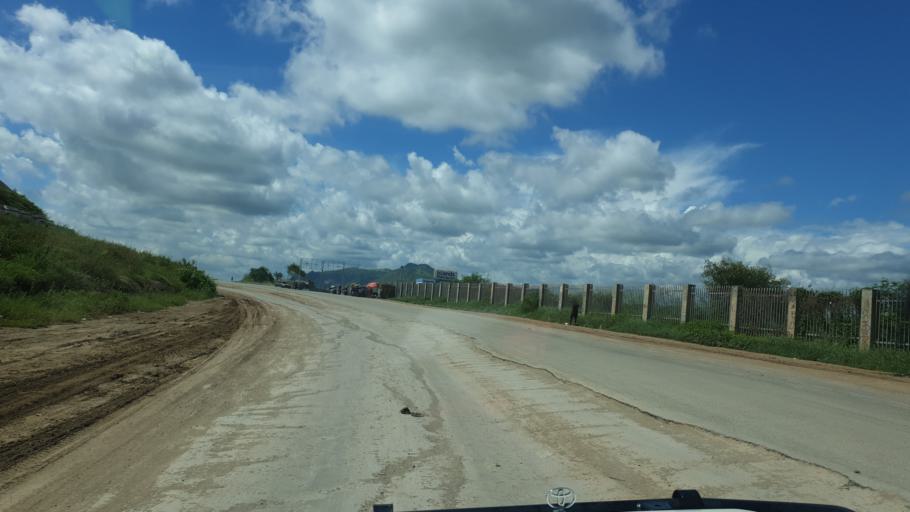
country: PG
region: National Capital
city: Port Moresby
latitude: -9.3989
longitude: 147.2298
